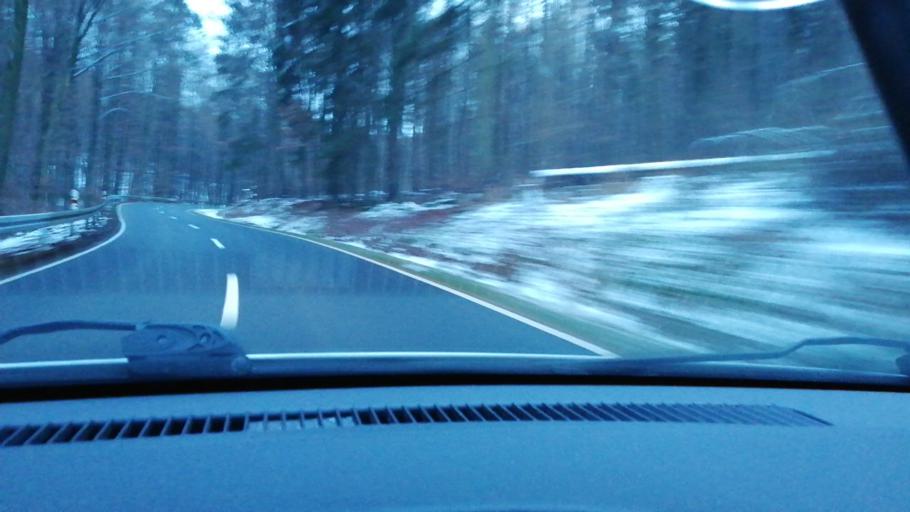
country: DE
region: Bavaria
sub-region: Regierungsbezirk Unterfranken
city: Geiselbach
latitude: 50.1355
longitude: 9.1836
